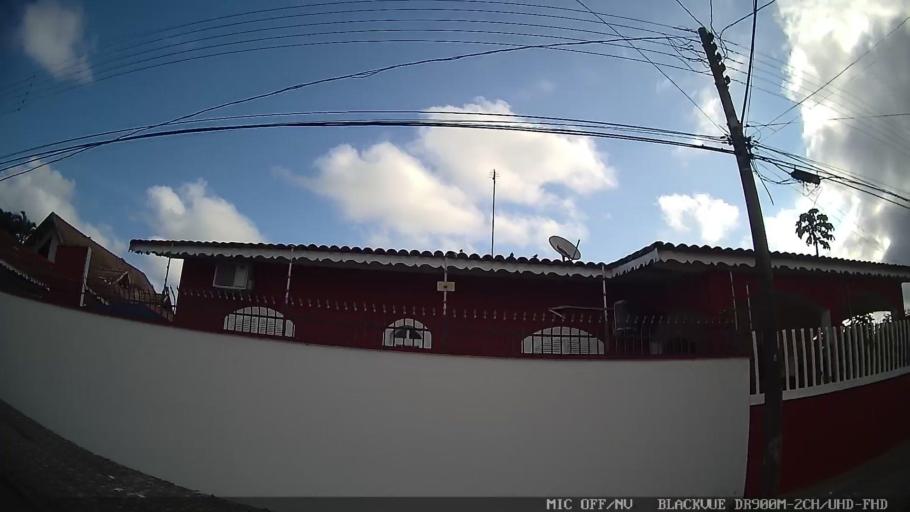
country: BR
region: Sao Paulo
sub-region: Peruibe
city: Peruibe
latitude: -24.3151
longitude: -46.9881
